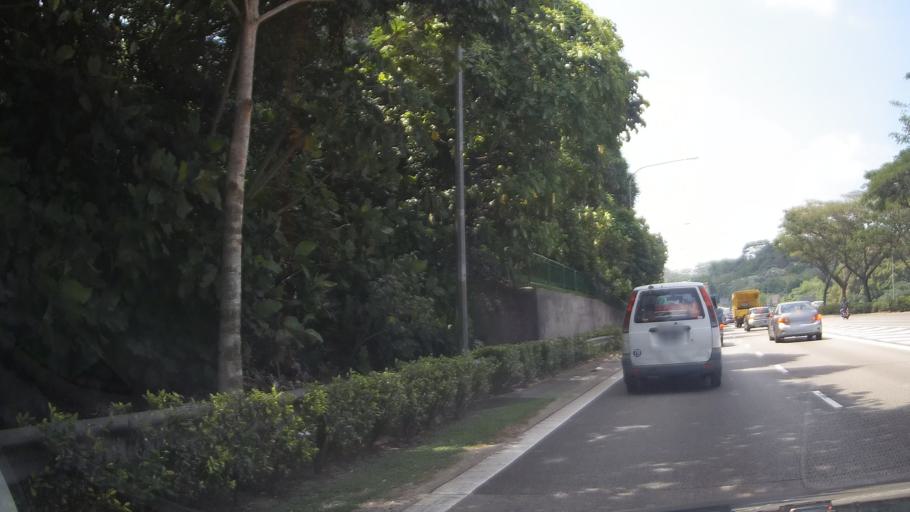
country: MY
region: Johor
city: Johor Bahru
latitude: 1.4185
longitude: 103.7716
